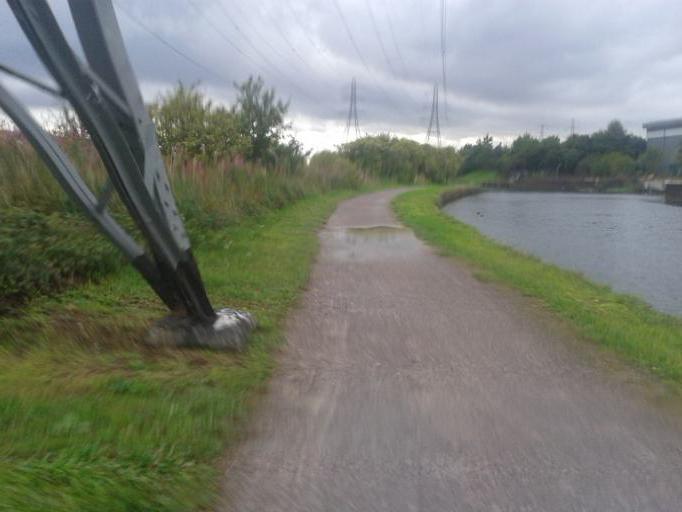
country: GB
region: England
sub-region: Essex
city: Waltham Abbey
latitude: 51.6553
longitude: -0.0202
